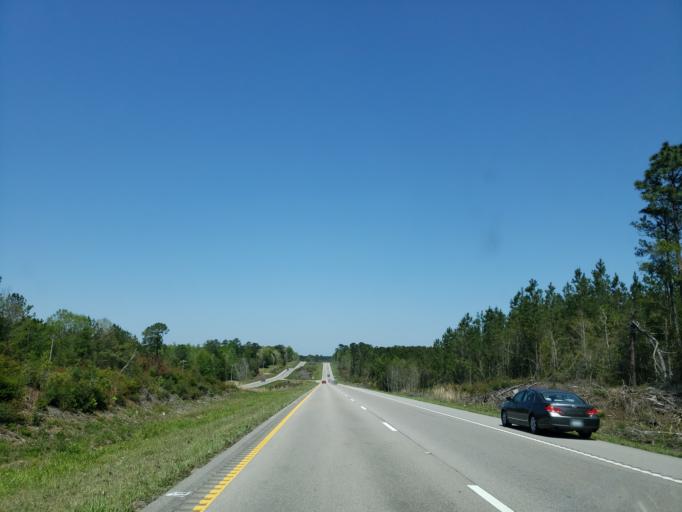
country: US
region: Mississippi
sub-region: Stone County
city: Wiggins
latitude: 30.9675
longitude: -89.1946
